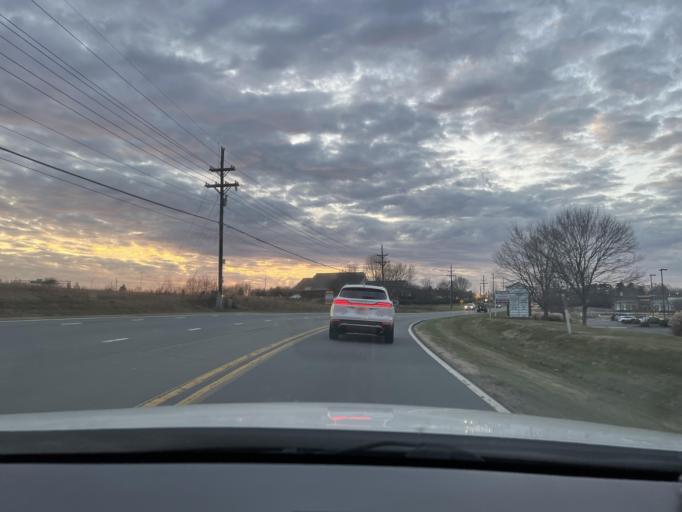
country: US
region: North Carolina
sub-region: Guilford County
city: McLeansville
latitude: 36.0625
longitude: -79.6027
